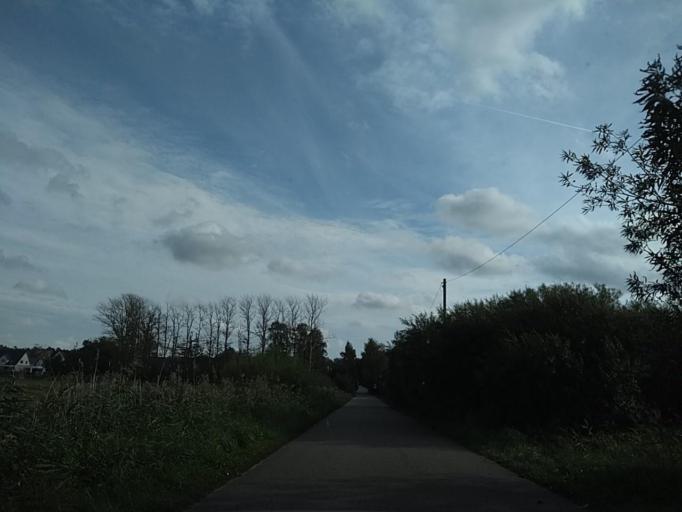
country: DE
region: Mecklenburg-Vorpommern
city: Seeheilbad Graal-Muritz
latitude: 54.2601
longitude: 12.2542
